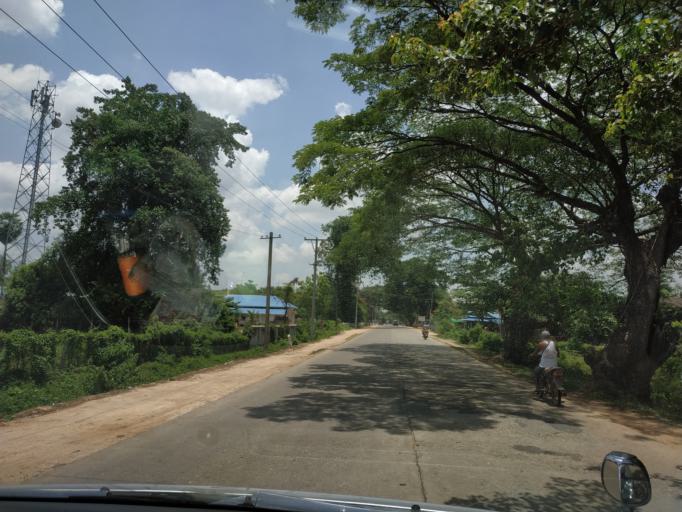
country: MM
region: Bago
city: Bago
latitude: 17.4761
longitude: 96.5141
